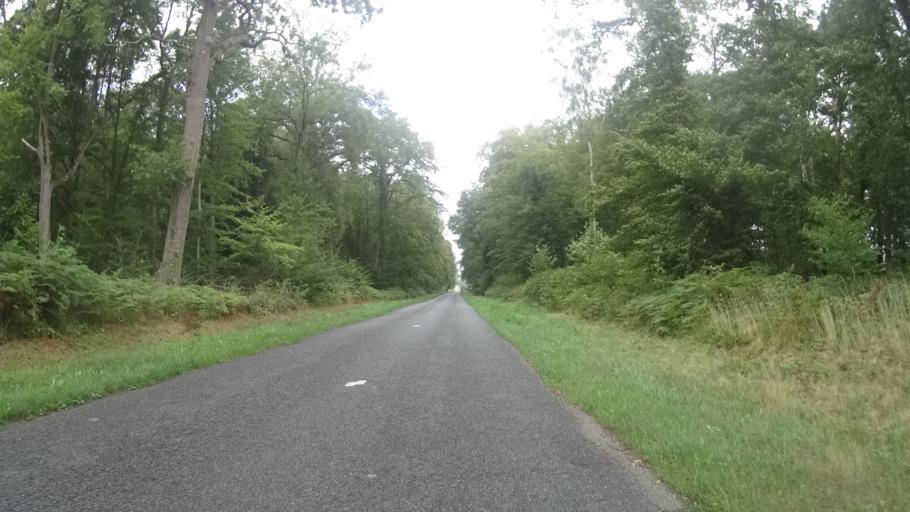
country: FR
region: Picardie
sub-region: Departement de l'Oise
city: Chiry-Ourscamp
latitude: 49.5464
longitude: 2.9848
